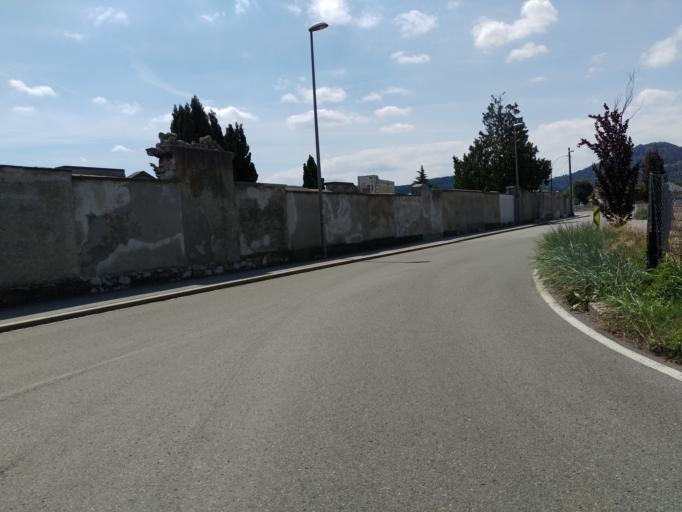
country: AT
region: Styria
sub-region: Graz Stadt
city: Wetzelsdorf
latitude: 47.0677
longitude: 15.4166
